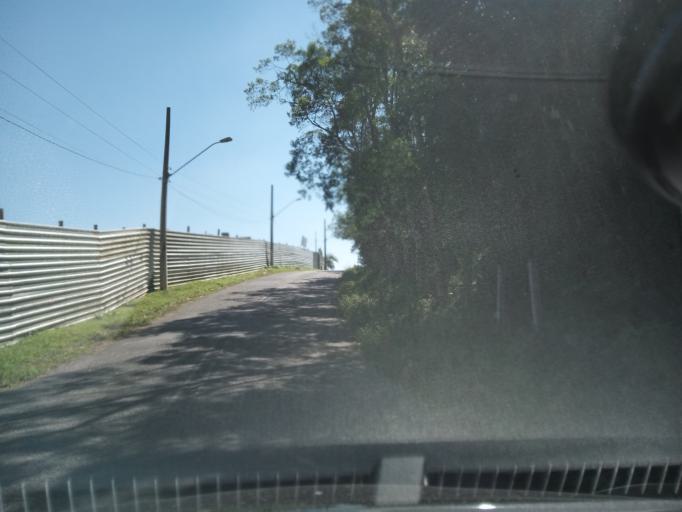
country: BR
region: Sao Paulo
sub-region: Sao Bernardo Do Campo
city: Sao Bernardo do Campo
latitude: -23.7963
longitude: -46.5392
